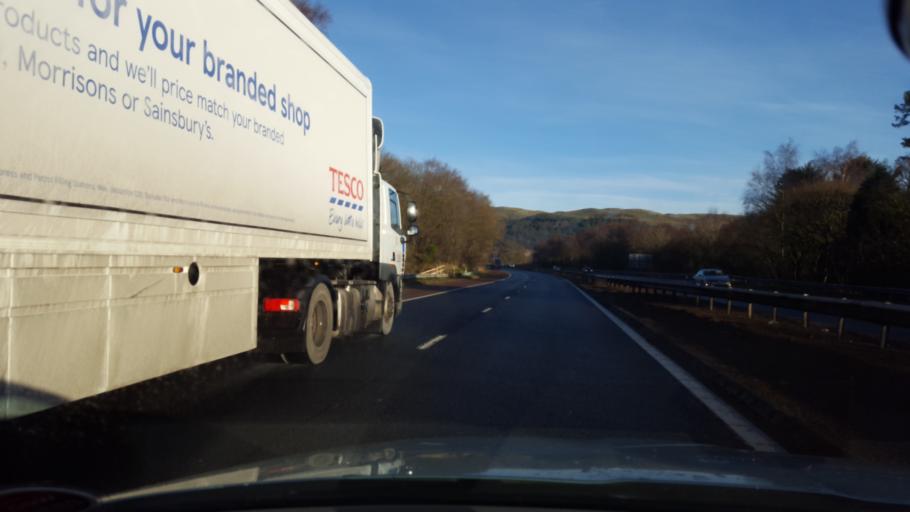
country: GB
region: Scotland
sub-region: Fife
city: Kelty
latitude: 56.1427
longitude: -3.3951
